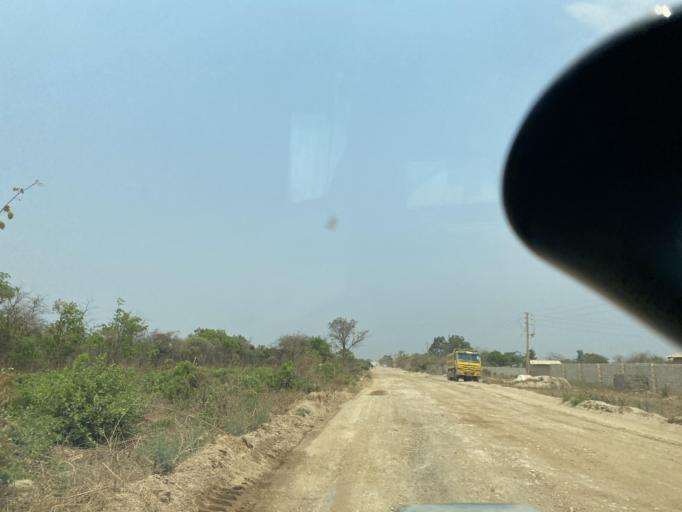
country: ZM
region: Lusaka
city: Lusaka
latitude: -15.5223
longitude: 28.3421
